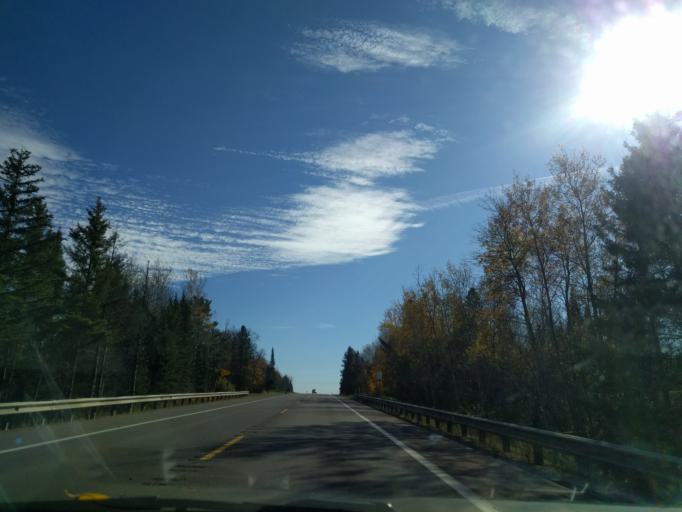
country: US
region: Michigan
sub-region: Marquette County
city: West Ishpeming
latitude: 46.3604
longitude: -87.9851
